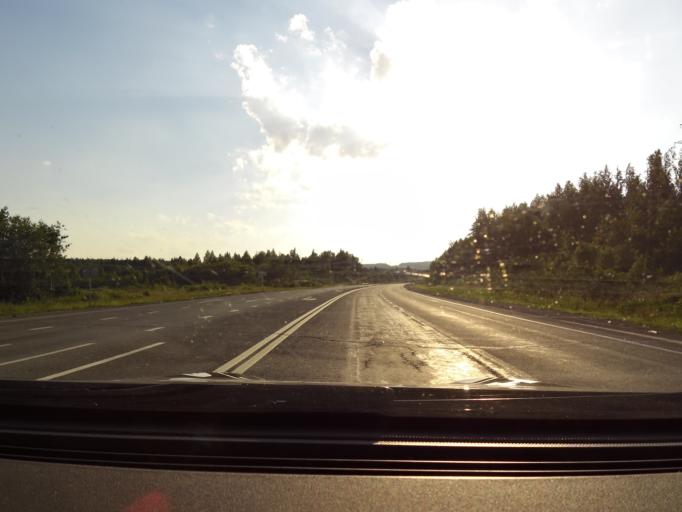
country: RU
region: Sverdlovsk
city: Revda
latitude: 56.8263
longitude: 59.8786
